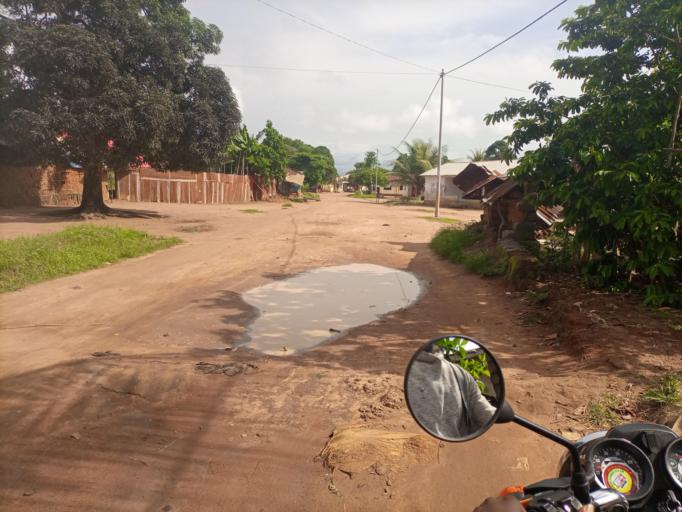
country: SL
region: Northern Province
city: Masoyila
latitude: 8.6118
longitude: -13.1715
